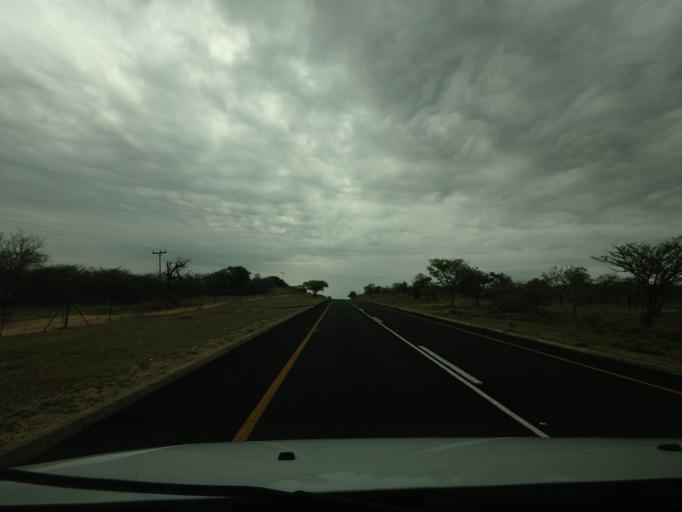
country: ZA
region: Limpopo
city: Thulamahashi
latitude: -24.5643
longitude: 31.1277
